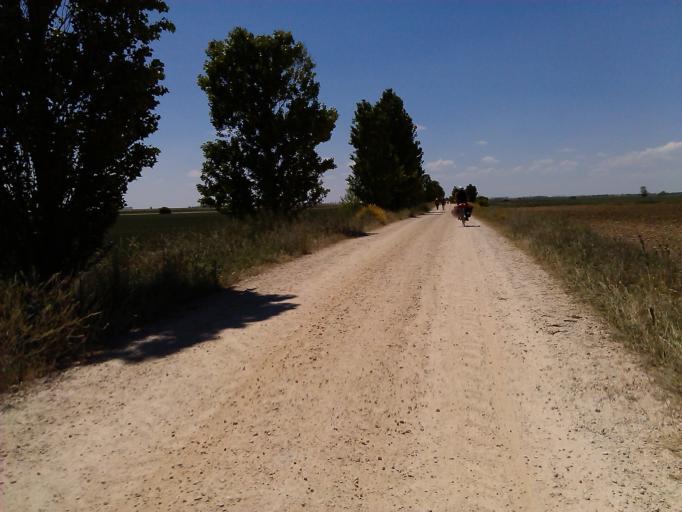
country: ES
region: Castille and Leon
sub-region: Provincia de Palencia
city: Bustillo del Paramo de Carrion
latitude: 42.3377
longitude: -4.7220
